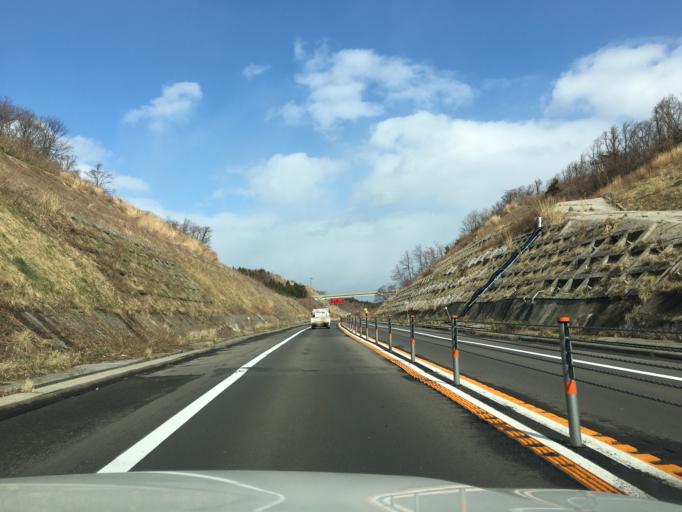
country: JP
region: Akita
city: Akita Shi
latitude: 39.4732
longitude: 140.0550
